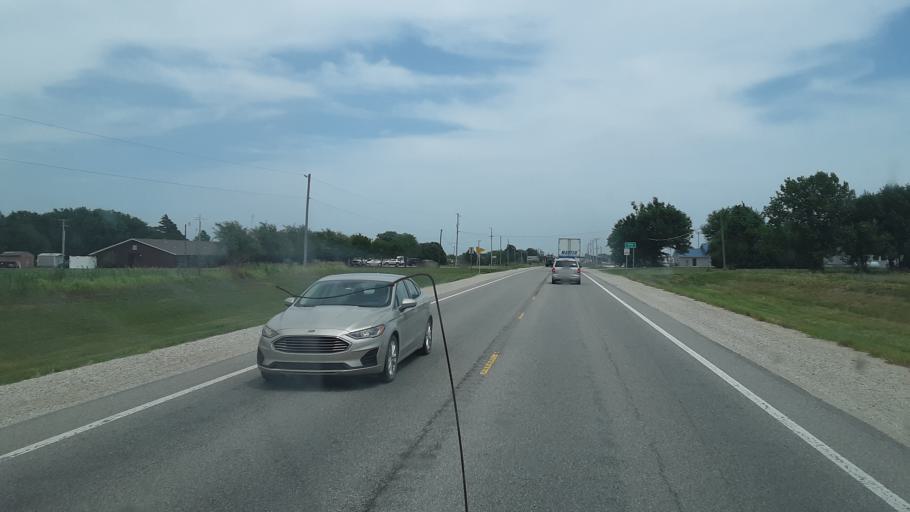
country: US
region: Kansas
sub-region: Allen County
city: Iola
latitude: 37.9216
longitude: -95.1771
